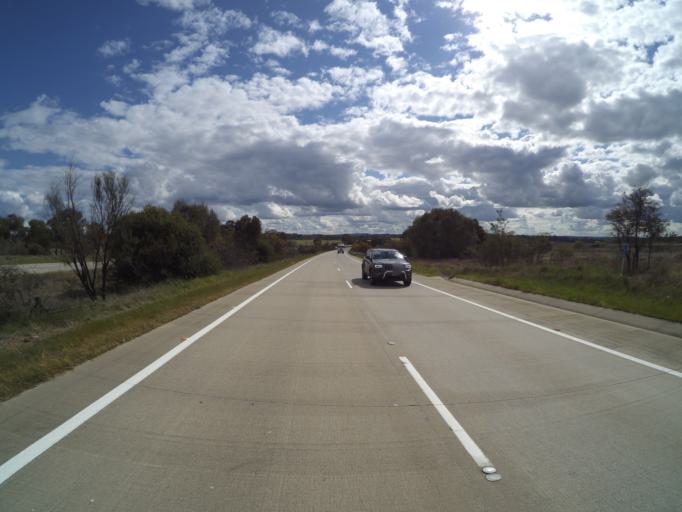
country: AU
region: New South Wales
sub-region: Yass Valley
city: Murrumbateman
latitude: -34.7883
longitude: 149.1972
